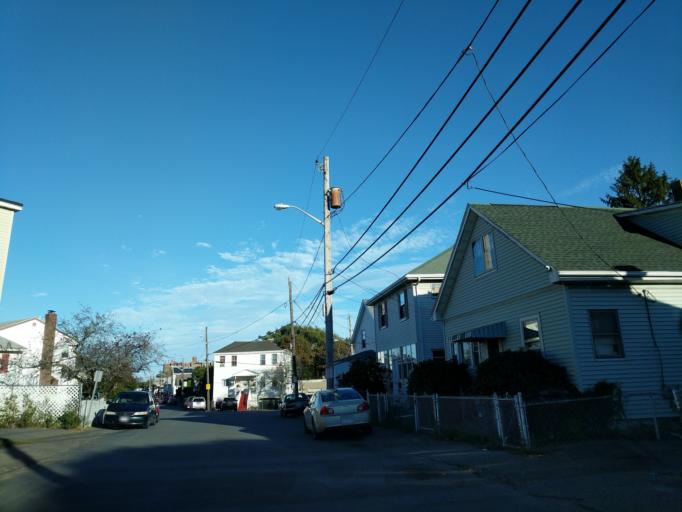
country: US
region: Massachusetts
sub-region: Suffolk County
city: Revere
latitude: 42.4014
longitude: -70.9964
